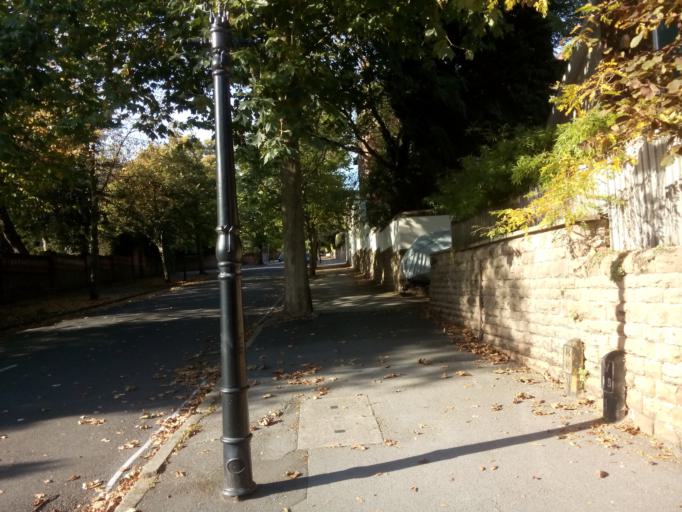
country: GB
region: England
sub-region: Nottingham
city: Nottingham
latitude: 52.9488
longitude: -1.1622
